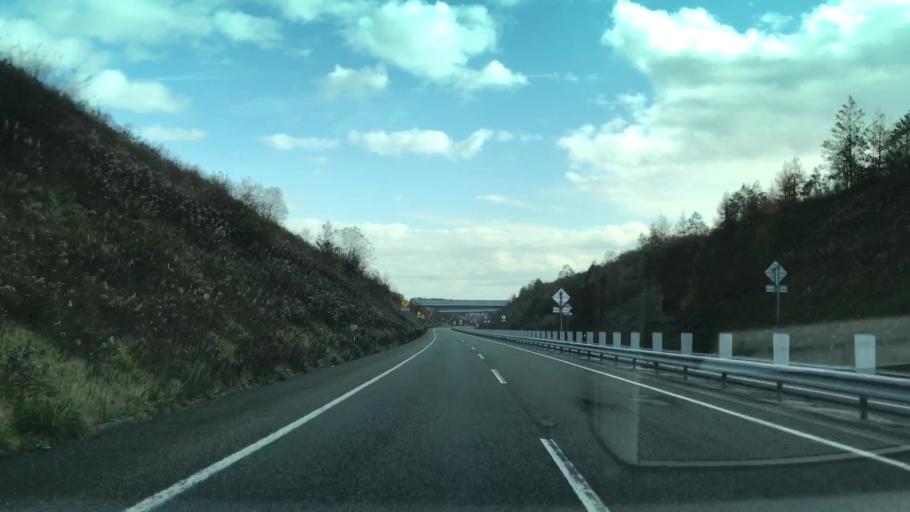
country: JP
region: Hokkaido
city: Tomakomai
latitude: 42.5435
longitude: 142.0044
